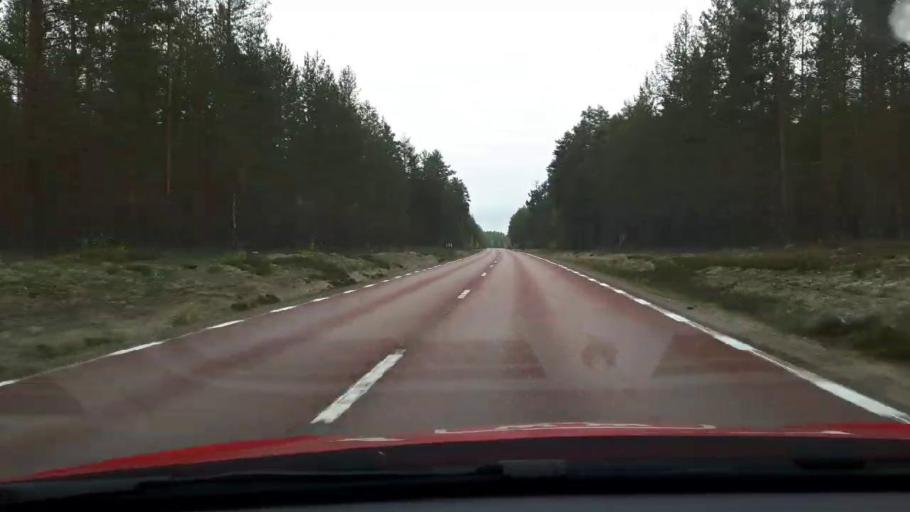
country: SE
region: Gaevleborg
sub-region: Ljusdals Kommun
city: Farila
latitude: 61.8307
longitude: 15.7518
